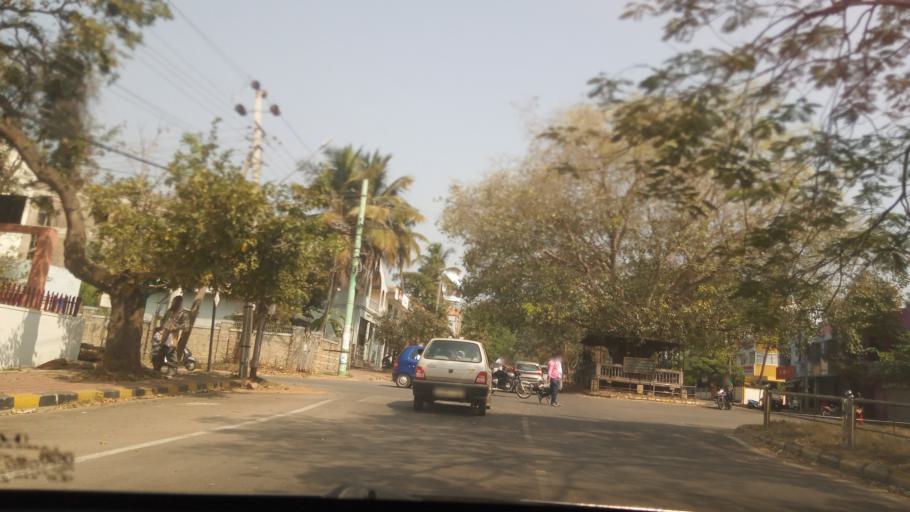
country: IN
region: Karnataka
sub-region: Mysore
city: Mysore
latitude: 12.2996
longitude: 76.6261
